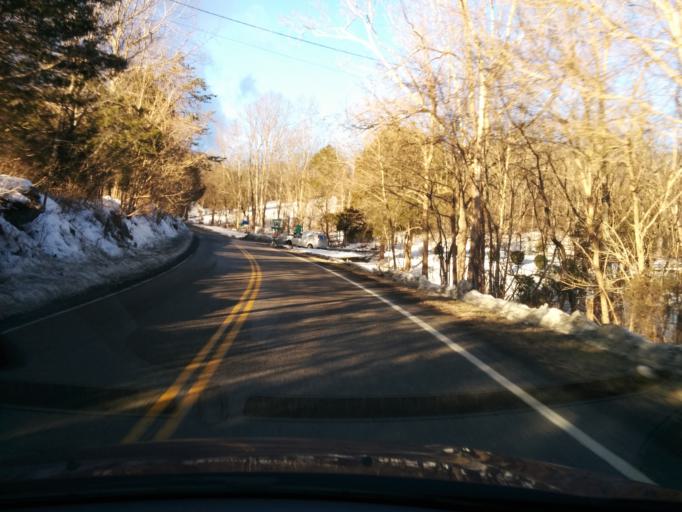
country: US
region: Virginia
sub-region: City of Lexington
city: Lexington
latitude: 37.7449
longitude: -79.5285
